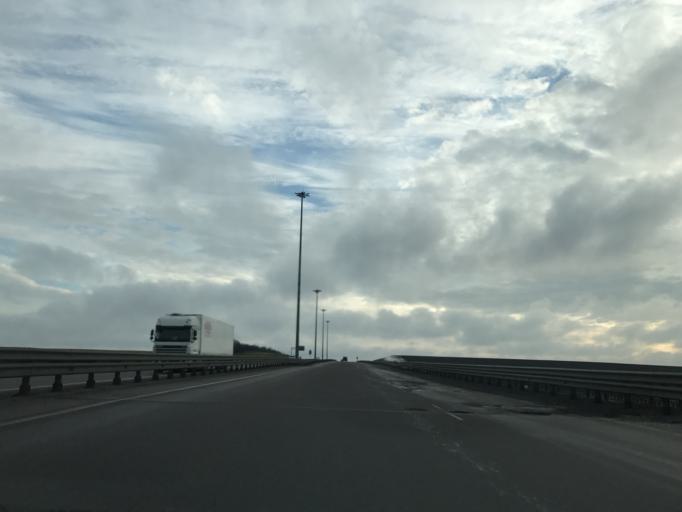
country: RU
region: Rostov
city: Glubokiy
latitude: 48.4501
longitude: 40.3409
